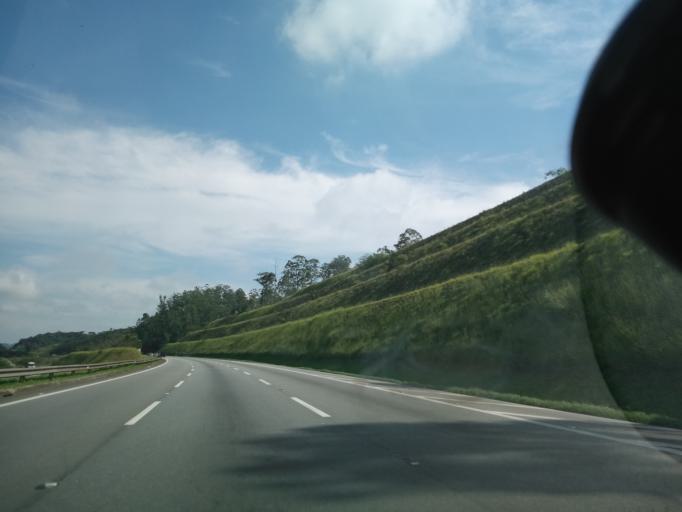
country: BR
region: Sao Paulo
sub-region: Itapecerica Da Serra
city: Itapecerica da Serra
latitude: -23.6861
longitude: -46.8187
